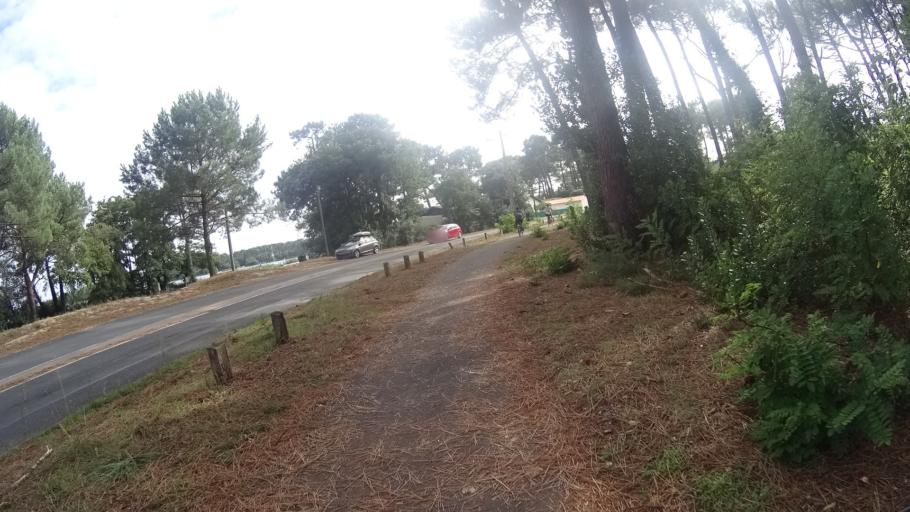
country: FR
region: Aquitaine
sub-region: Departement de la Gironde
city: Lacanau
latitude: 44.9969
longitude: -1.1422
